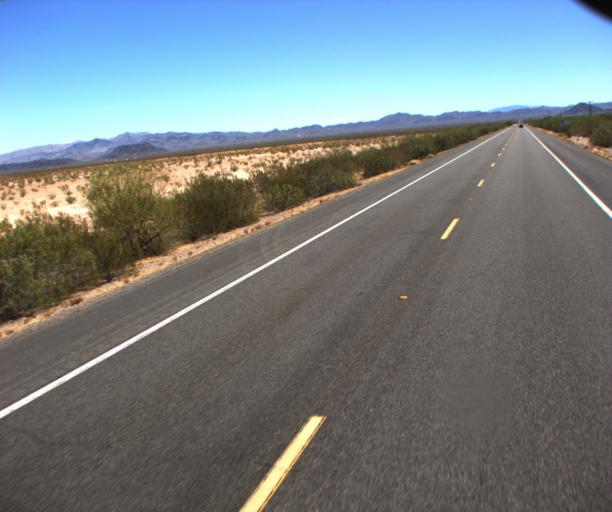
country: US
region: Arizona
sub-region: La Paz County
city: Salome
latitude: 33.7014
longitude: -113.8510
